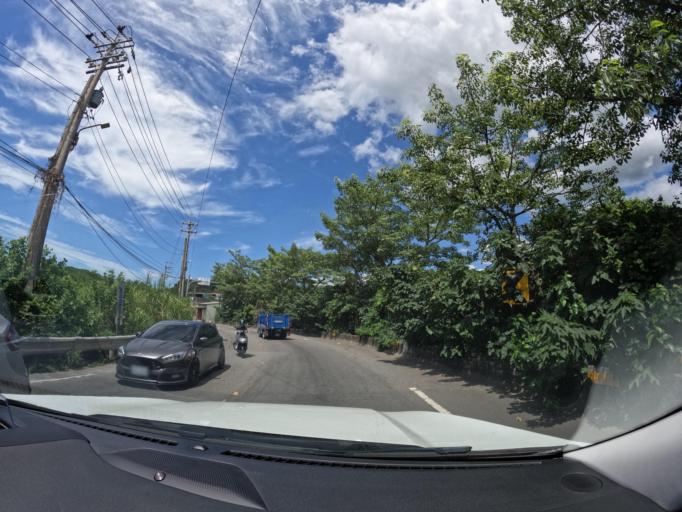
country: TW
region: Taipei
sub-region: Taipei
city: Banqiao
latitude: 25.1282
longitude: 121.3921
